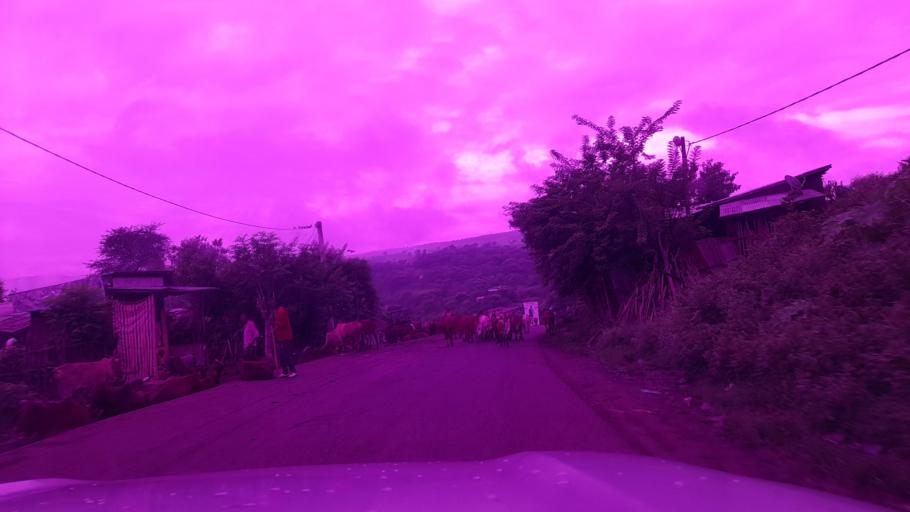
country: ET
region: Oromiya
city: Waliso
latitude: 8.2274
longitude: 37.5766
